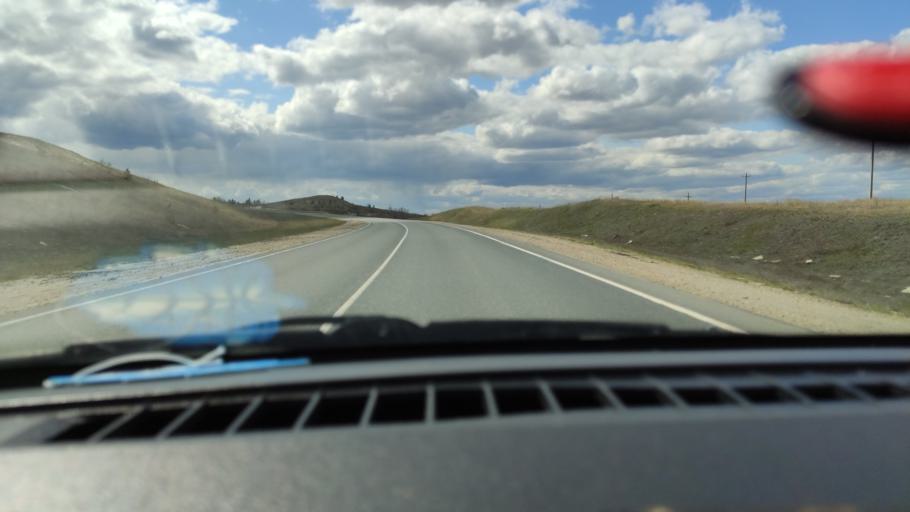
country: RU
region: Saratov
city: Alekseyevka
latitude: 52.3244
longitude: 47.9208
